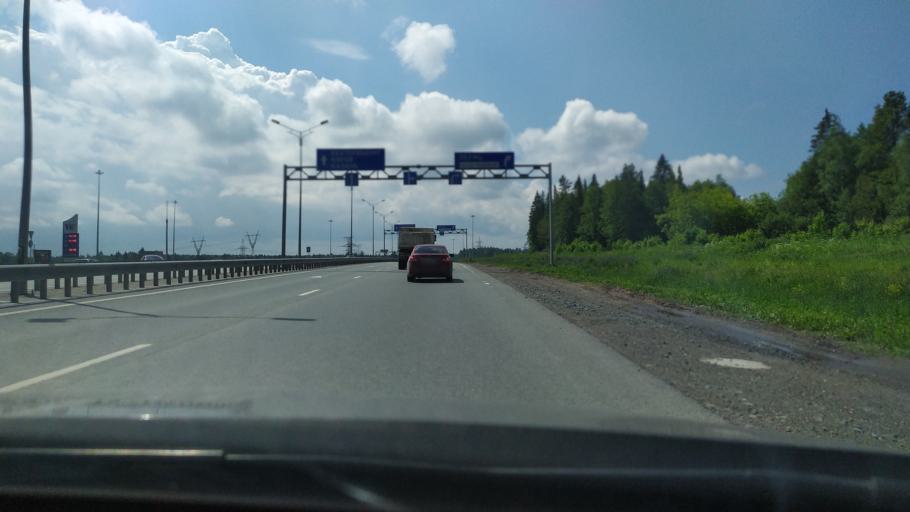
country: RU
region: Perm
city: Ferma
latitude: 58.0024
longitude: 56.3902
